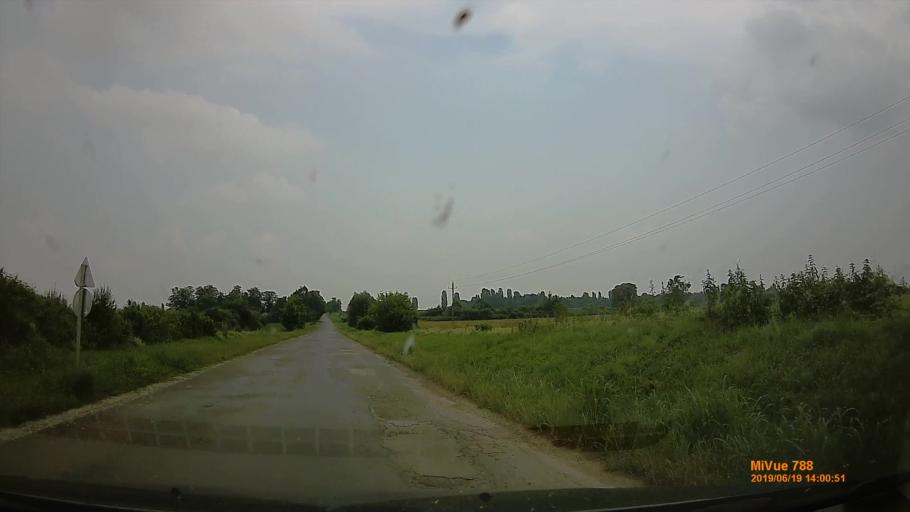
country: HU
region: Baranya
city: Szigetvar
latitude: 46.0822
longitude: 17.8084
